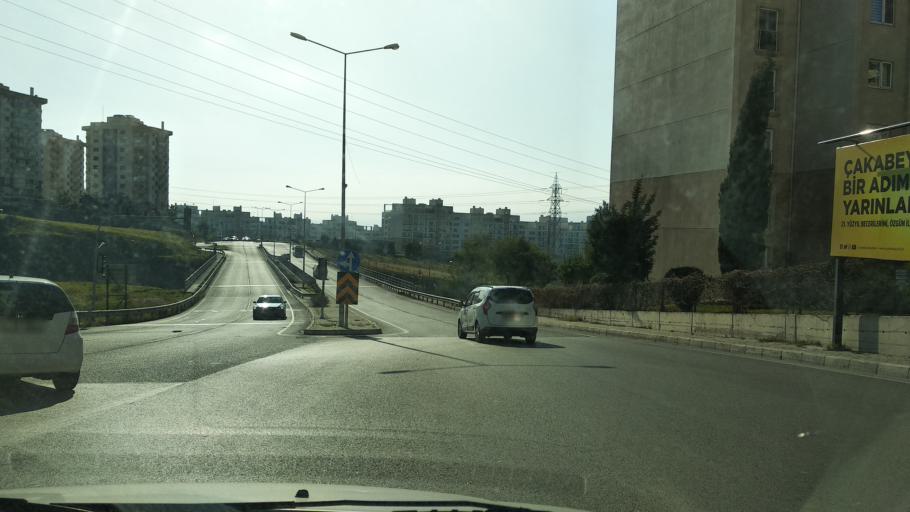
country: TR
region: Izmir
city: Karsiyaka
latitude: 38.4908
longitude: 27.0909
